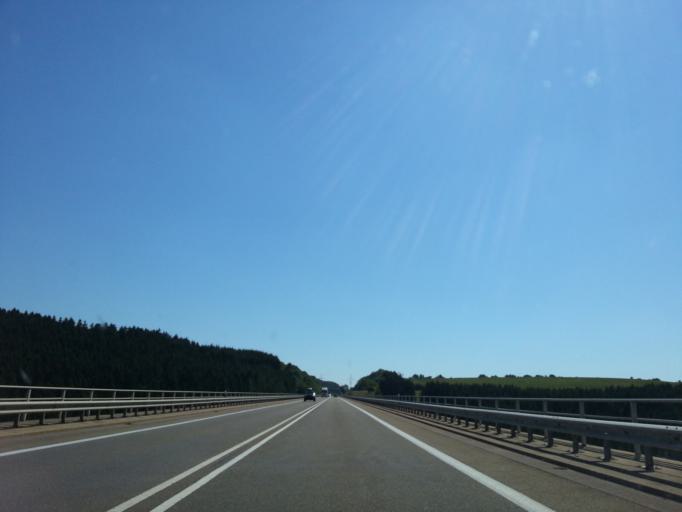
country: DE
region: Rheinland-Pfalz
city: Pittenbach
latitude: 50.2015
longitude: 6.3508
